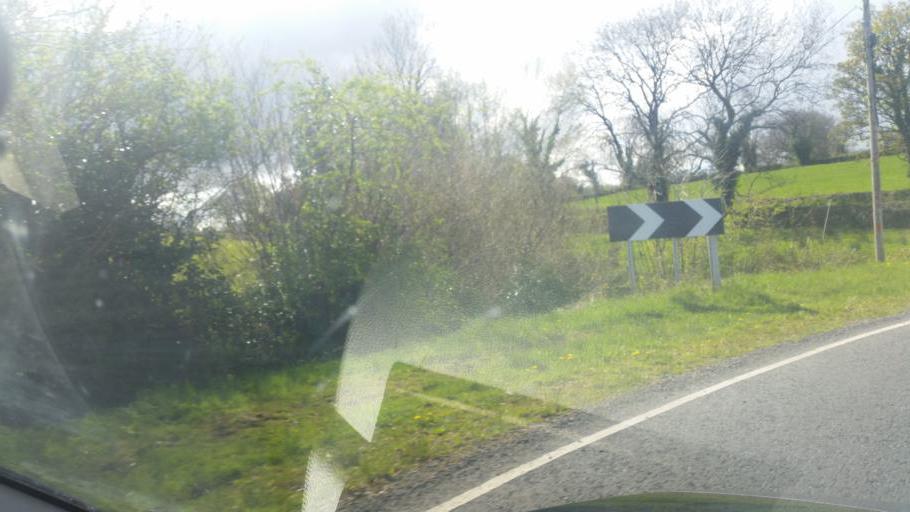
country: GB
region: Northern Ireland
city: Irvinestown
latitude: 54.4501
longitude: -7.8072
